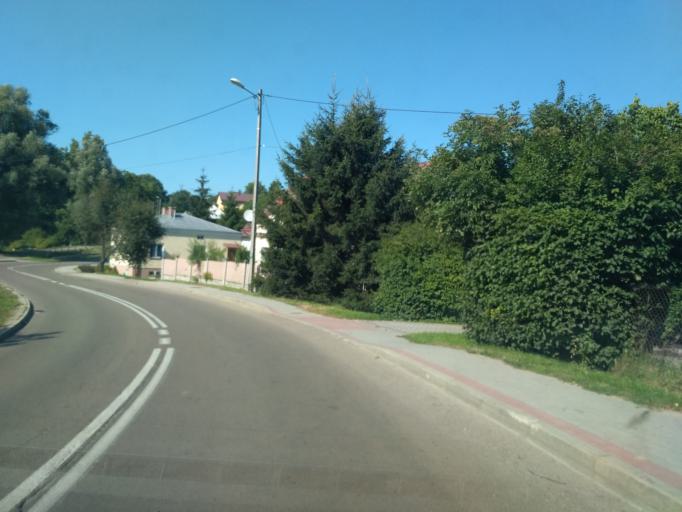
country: PL
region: Subcarpathian Voivodeship
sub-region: Krosno
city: Krosno
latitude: 49.6729
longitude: 21.7664
